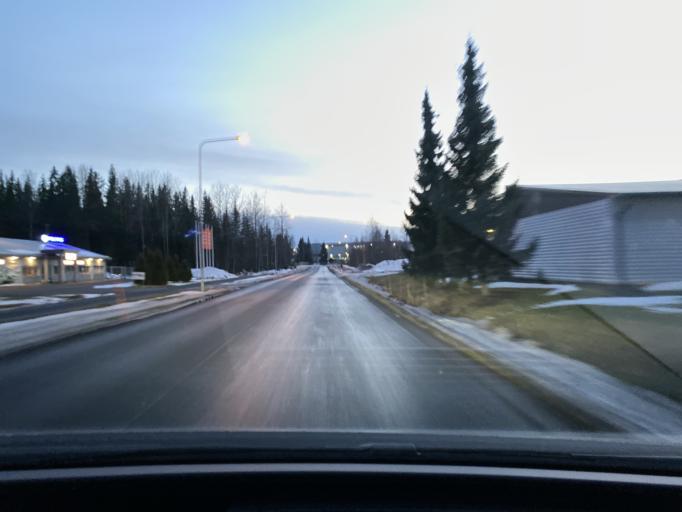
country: FI
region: Varsinais-Suomi
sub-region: Loimaa
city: Loimaa
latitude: 60.8433
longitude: 23.0222
